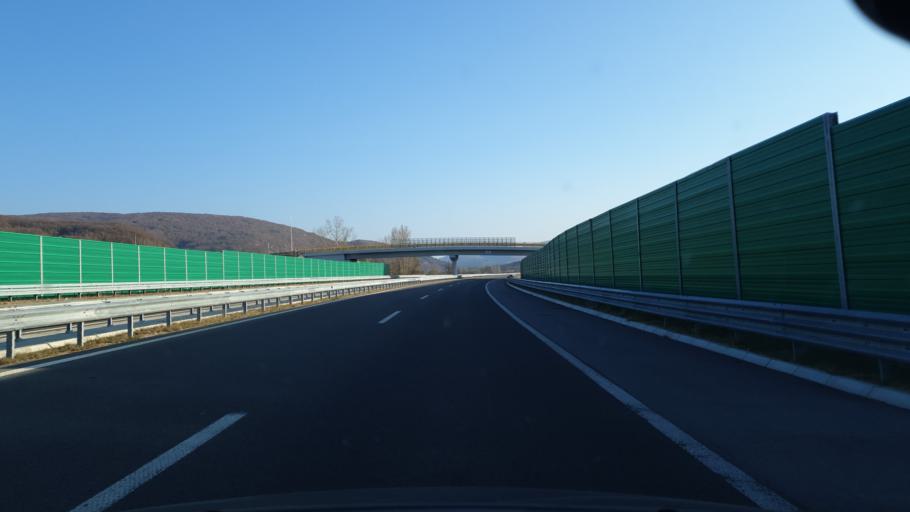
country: RS
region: Central Serbia
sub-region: Pirotski Okrug
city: Dimitrovgrad
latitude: 43.0464
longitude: 22.7054
